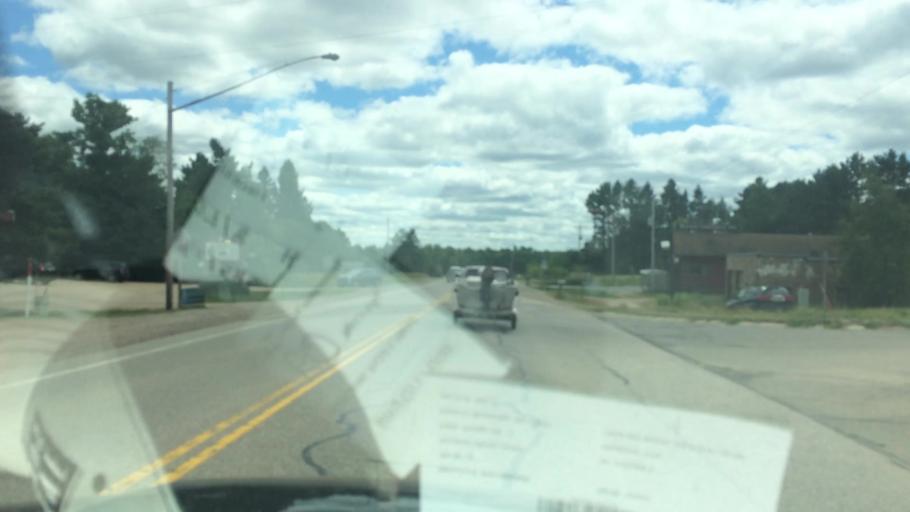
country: US
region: Wisconsin
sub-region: Vilas County
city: Eagle River
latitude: 45.7902
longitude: -89.3206
